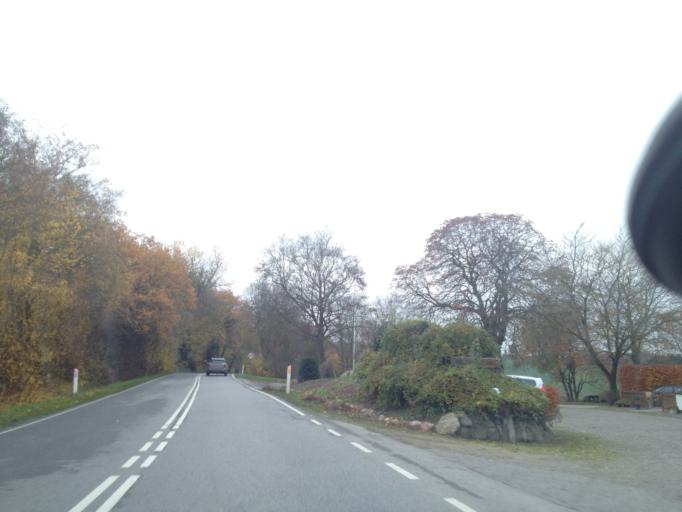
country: DK
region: South Denmark
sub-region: Assens Kommune
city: Vissenbjerg
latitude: 55.4494
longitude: 10.1346
